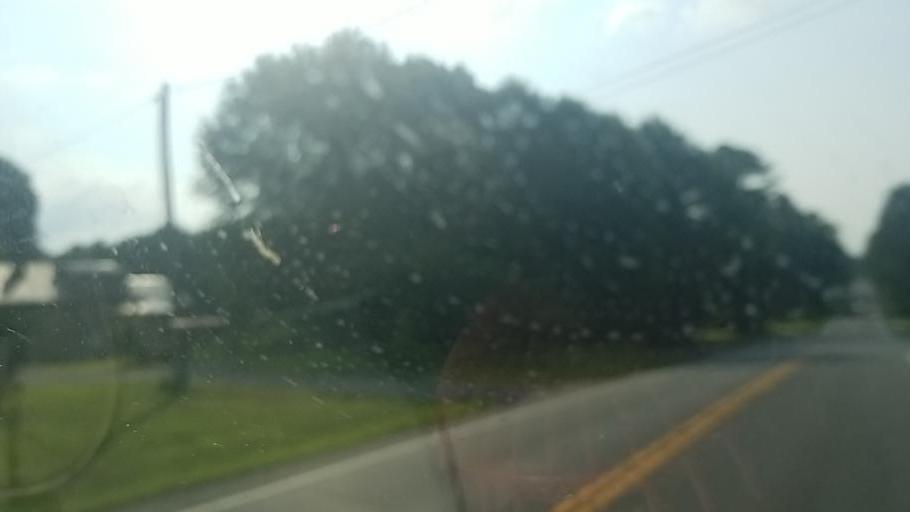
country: US
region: New York
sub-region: Fulton County
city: Broadalbin
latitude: 43.0714
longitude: -74.2535
